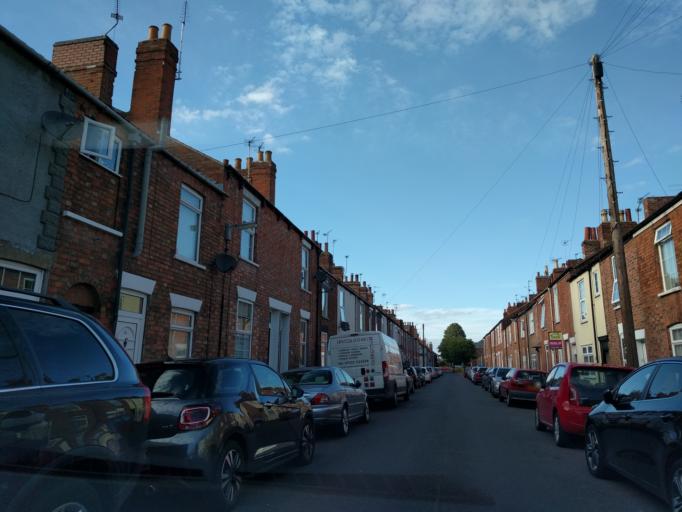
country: GB
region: England
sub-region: Nottinghamshire
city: Newark on Trent
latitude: 53.0722
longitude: -0.8026
